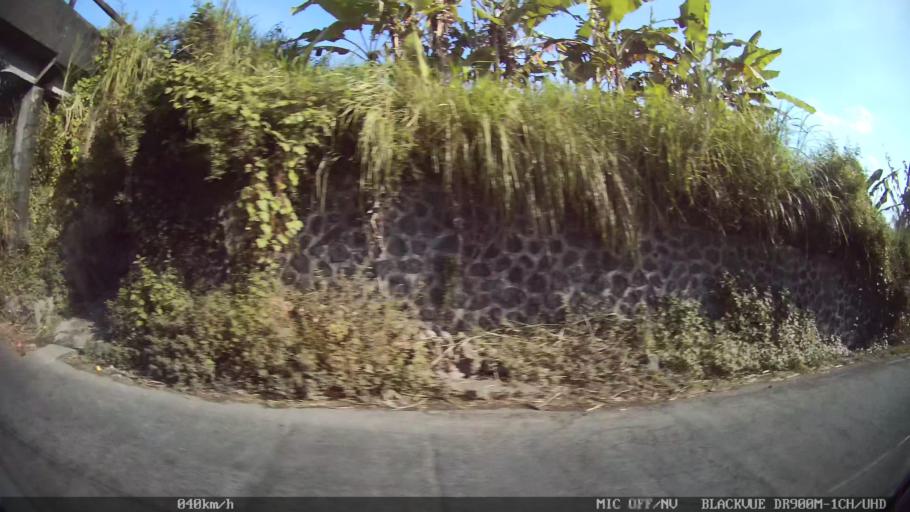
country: ID
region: Bali
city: Banjar Parekan
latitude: -8.5796
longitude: 115.2271
